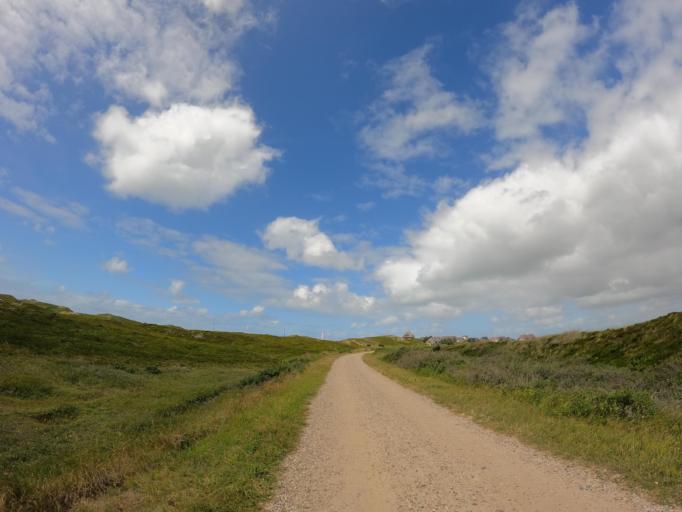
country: DE
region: Schleswig-Holstein
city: Westerland
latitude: 54.8380
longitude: 8.2941
